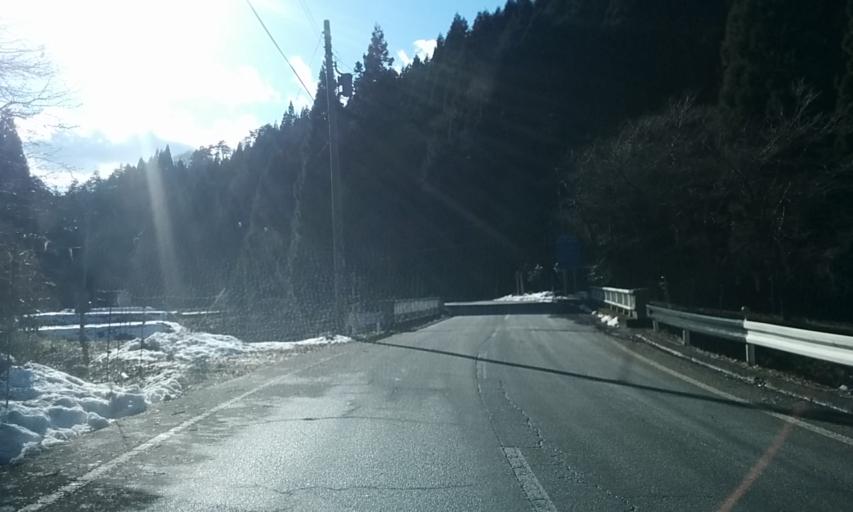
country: JP
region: Hyogo
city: Toyooka
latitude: 35.4236
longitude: 134.9634
